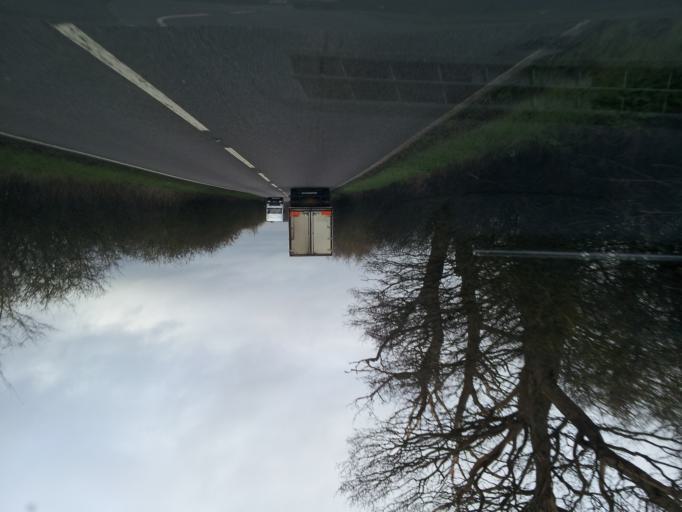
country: GB
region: England
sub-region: Norfolk
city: Diss
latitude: 52.3529
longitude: 1.1397
